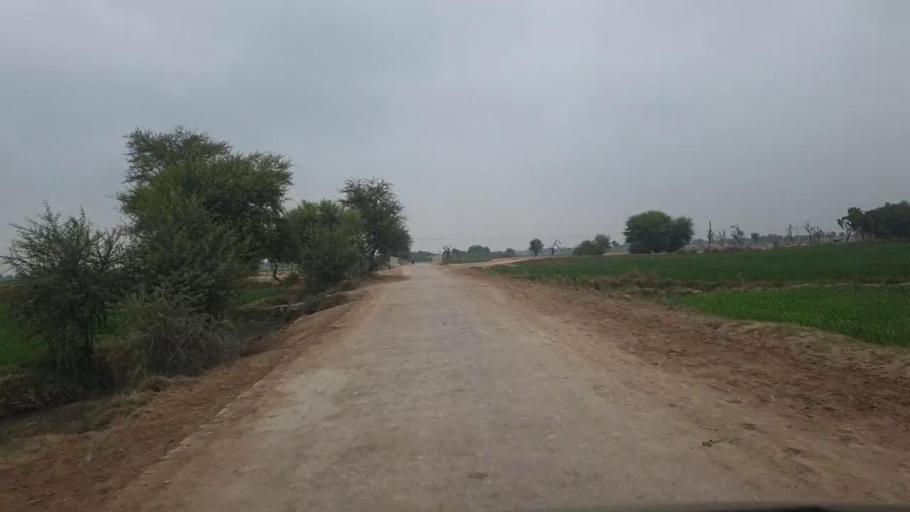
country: PK
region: Sindh
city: Shahdadpur
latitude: 25.9550
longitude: 68.7239
